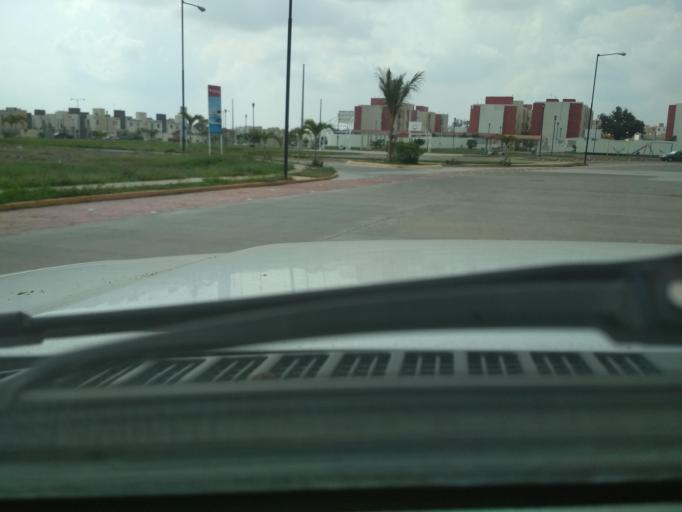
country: MX
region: Veracruz
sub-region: Veracruz
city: Lomas de Rio Medio Cuatro
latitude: 19.1804
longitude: -96.2092
